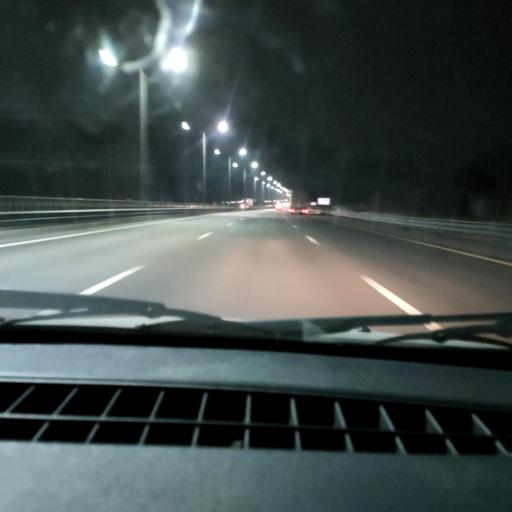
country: RU
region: Voronezj
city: Somovo
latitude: 51.7491
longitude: 39.3058
